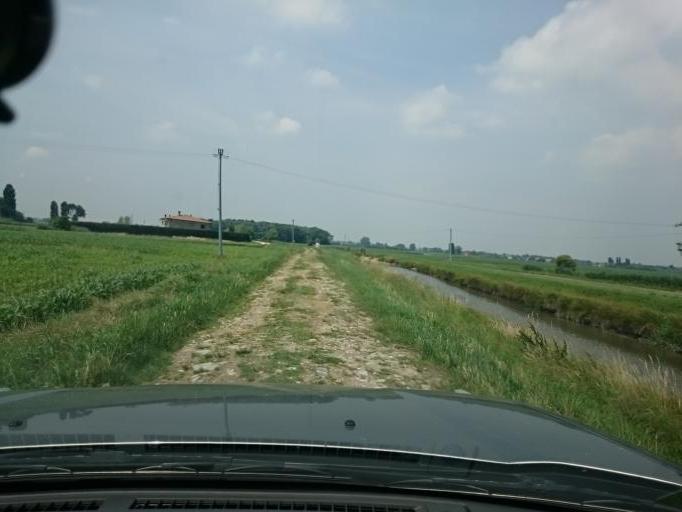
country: IT
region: Veneto
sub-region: Provincia di Padova
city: Correzzola
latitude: 45.2552
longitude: 12.0624
